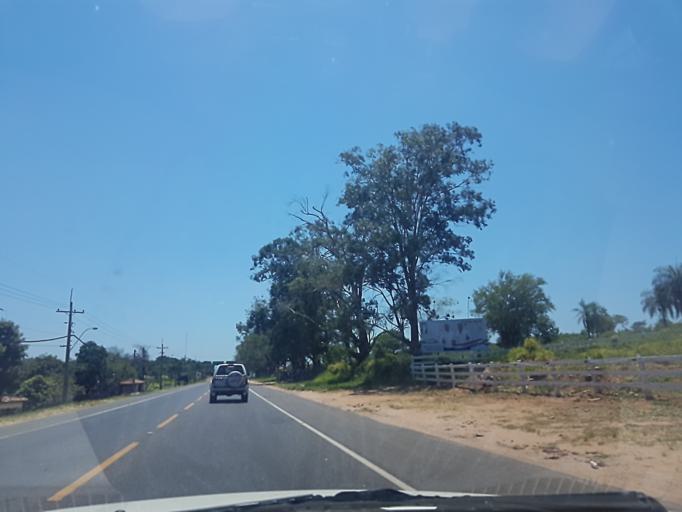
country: PY
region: Cordillera
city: Eusebio Ayala
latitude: -25.3844
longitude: -57.0528
